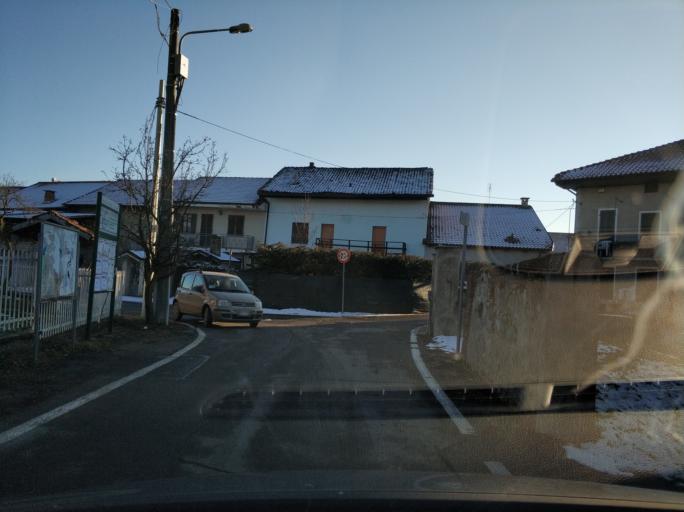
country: IT
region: Piedmont
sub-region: Provincia di Torino
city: San Francesco al Campo
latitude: 45.2286
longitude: 7.6553
